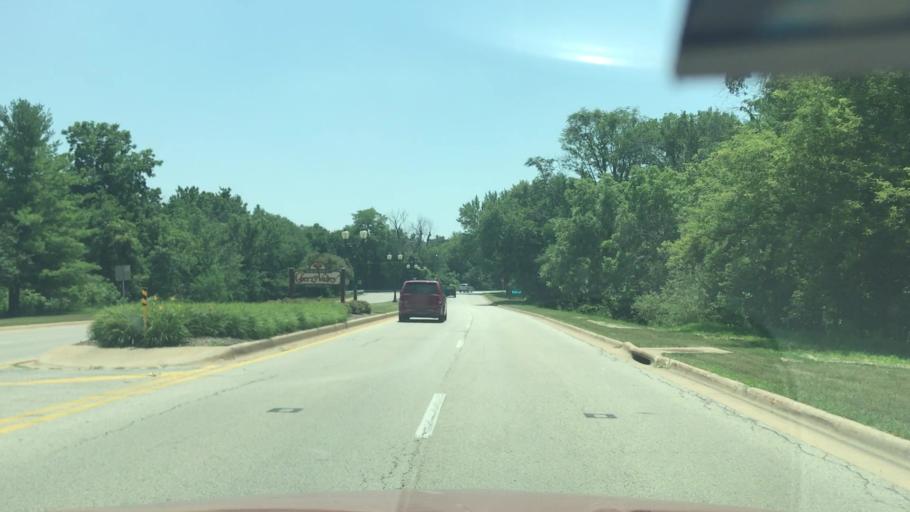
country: US
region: Illinois
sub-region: Winnebago County
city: Cherry Valley
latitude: 42.2381
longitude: -88.9559
